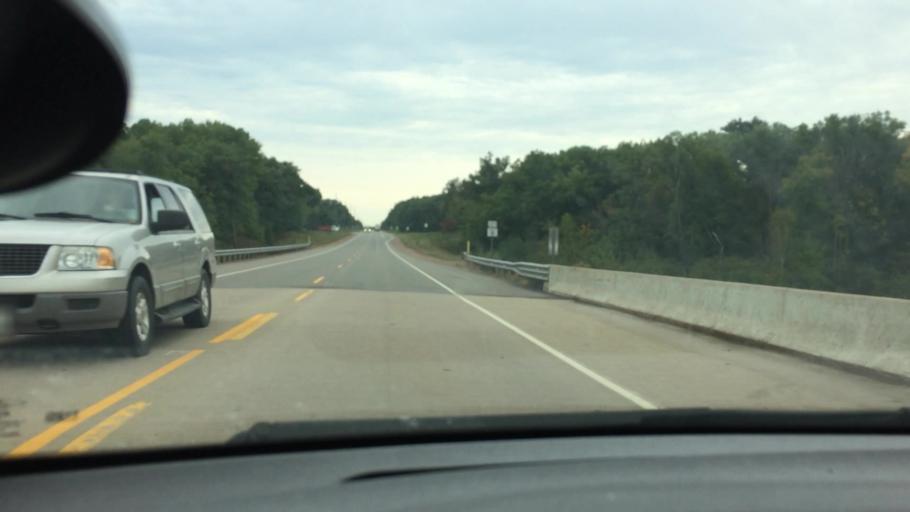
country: US
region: Wisconsin
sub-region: Clark County
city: Neillsville
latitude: 44.5706
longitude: -90.7273
